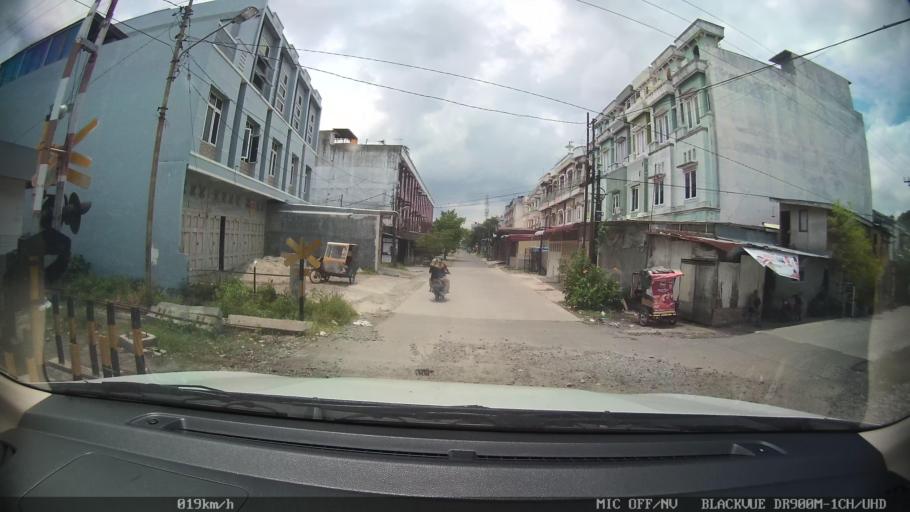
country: ID
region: North Sumatra
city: Medan
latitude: 3.6260
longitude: 98.6722
